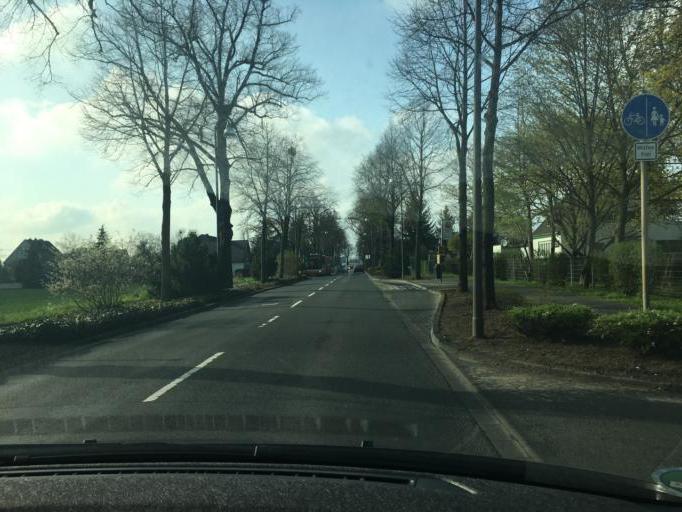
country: DE
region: North Rhine-Westphalia
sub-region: Regierungsbezirk Koln
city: Bonn
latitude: 50.7573
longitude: 7.0660
